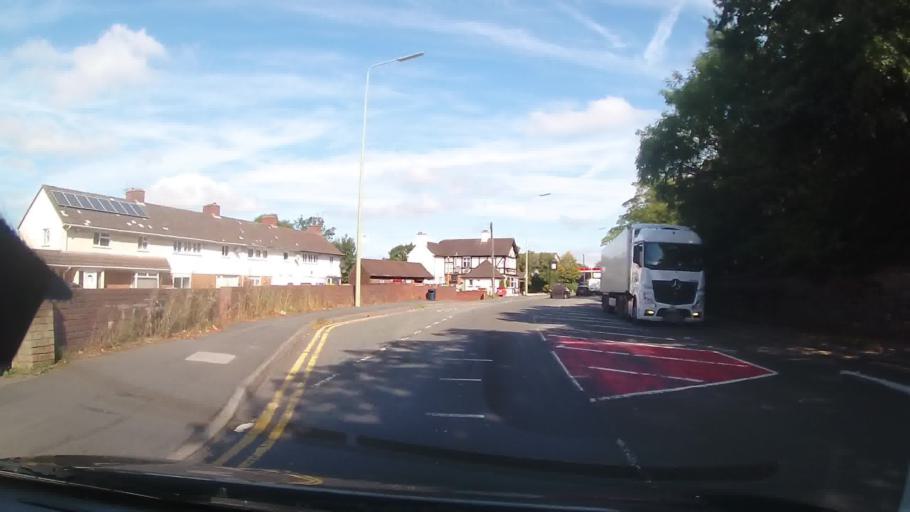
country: GB
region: England
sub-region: Staffordshire
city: Featherstone
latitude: 52.6436
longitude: -2.0867
